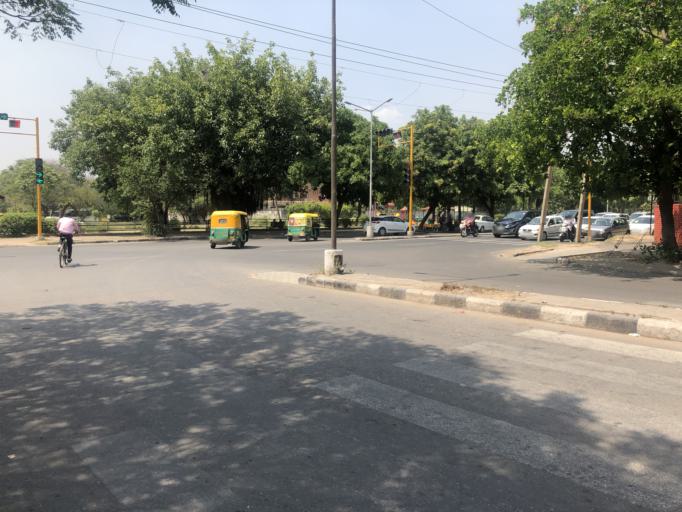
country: IN
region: Chandigarh
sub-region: Chandigarh
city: Chandigarh
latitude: 30.7092
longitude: 76.7558
